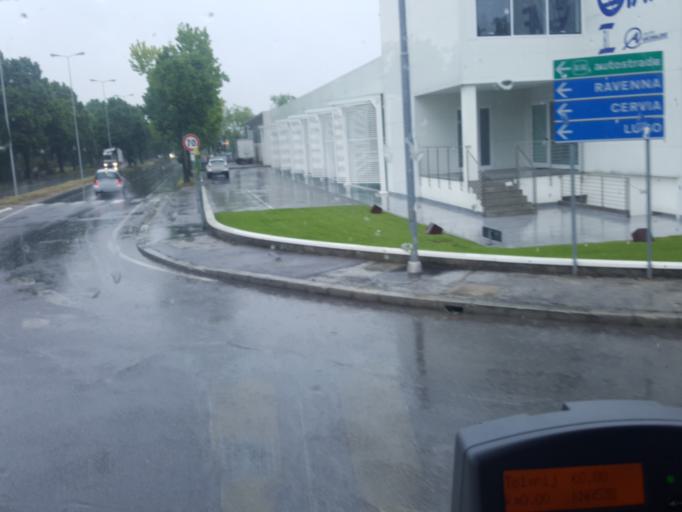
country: IT
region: Emilia-Romagna
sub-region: Forli-Cesena
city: Forli
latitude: 44.2322
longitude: 12.0796
